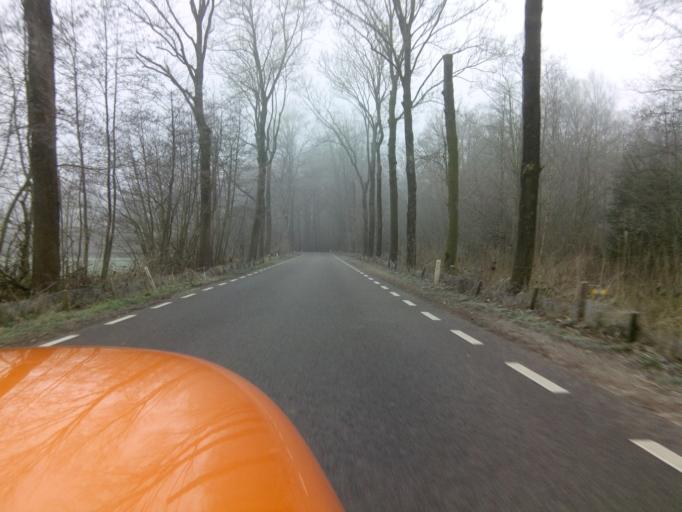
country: NL
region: Utrecht
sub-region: Gemeente Leusden
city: Leusden
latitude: 52.1577
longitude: 5.4598
